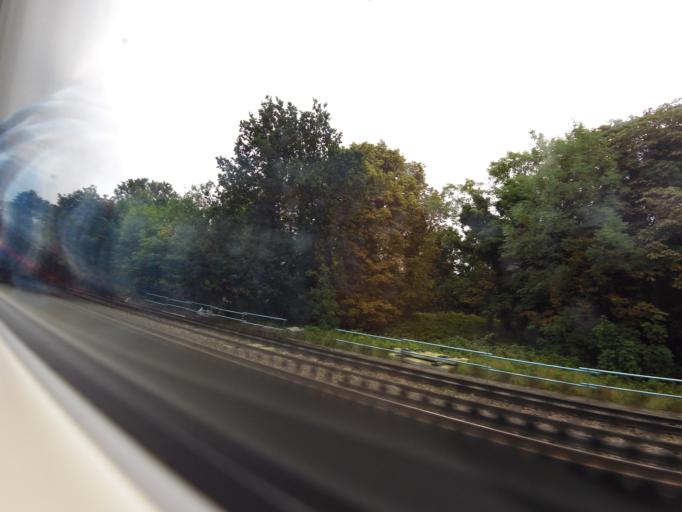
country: GB
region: England
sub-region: Greater London
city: Beckenham
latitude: 51.4219
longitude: -0.0571
